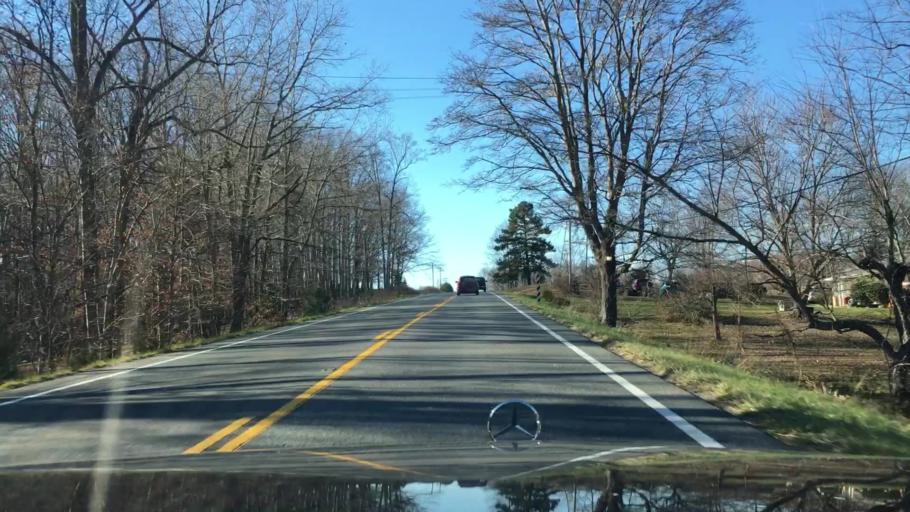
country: US
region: Virginia
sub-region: Franklin County
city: North Shore
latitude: 37.2414
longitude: -79.6672
